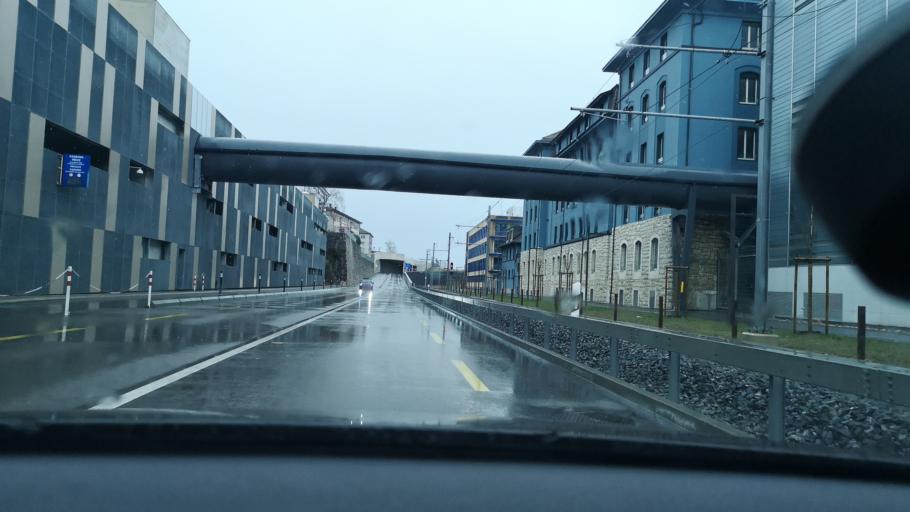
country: CH
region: Neuchatel
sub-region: Boudry District
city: Peseux
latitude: 46.9807
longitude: 6.8995
